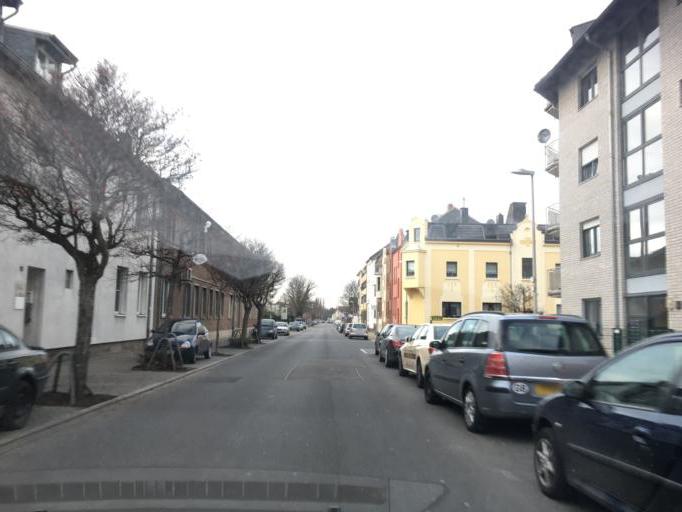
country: DE
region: North Rhine-Westphalia
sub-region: Regierungsbezirk Koln
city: Dueren
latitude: 50.8054
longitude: 6.4736
